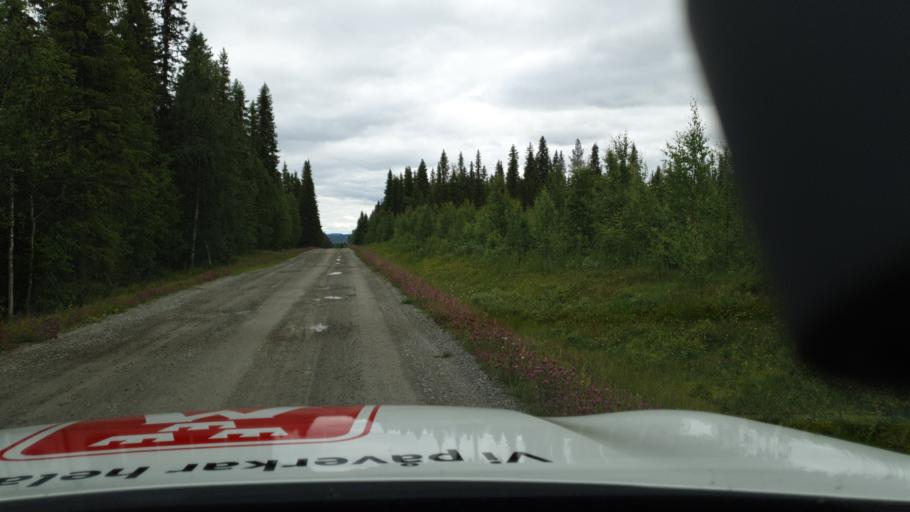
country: SE
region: Vaesterbotten
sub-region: Storumans Kommun
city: Storuman
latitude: 64.7696
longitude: 17.0480
